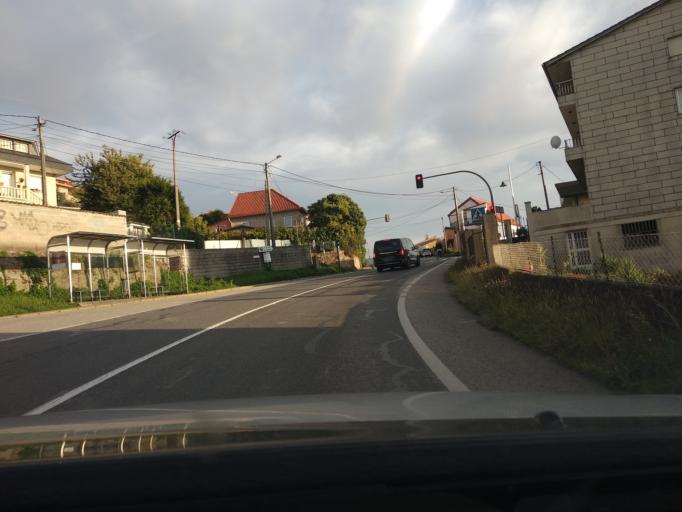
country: ES
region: Galicia
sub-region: Provincia de Pontevedra
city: Moana
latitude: 42.2815
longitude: -8.7113
